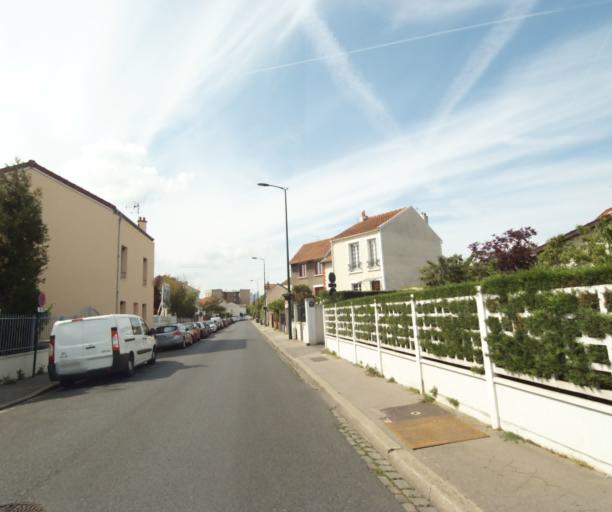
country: FR
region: Ile-de-France
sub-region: Departement des Hauts-de-Seine
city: Colombes
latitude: 48.9171
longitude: 2.2482
